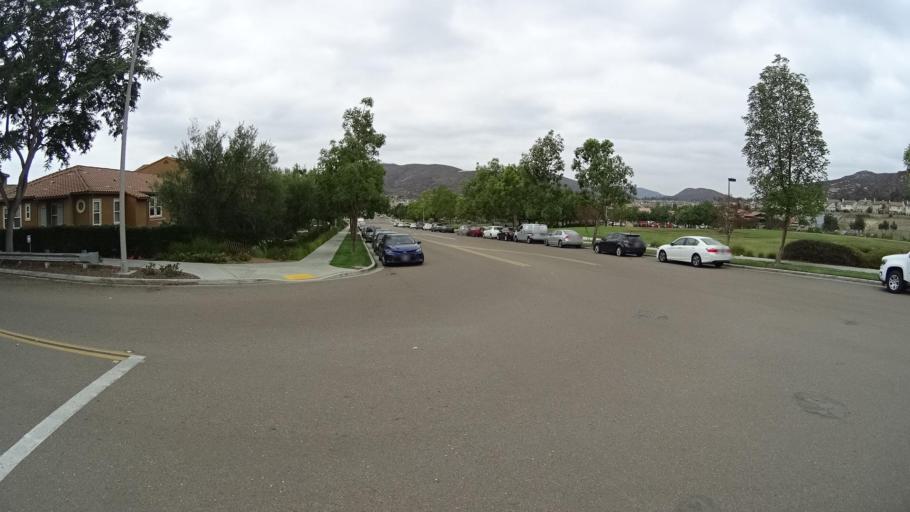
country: US
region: California
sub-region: San Diego County
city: Fairbanks Ranch
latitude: 33.0246
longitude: -117.1085
